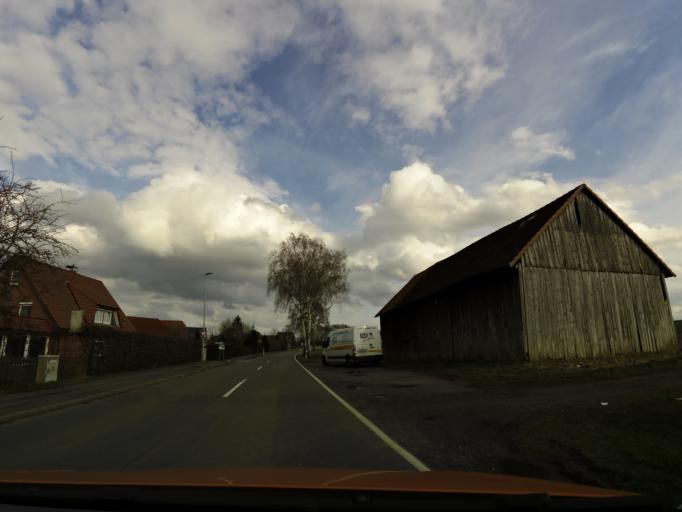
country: DE
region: Lower Saxony
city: Sudwalde
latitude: 52.8388
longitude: 8.8494
